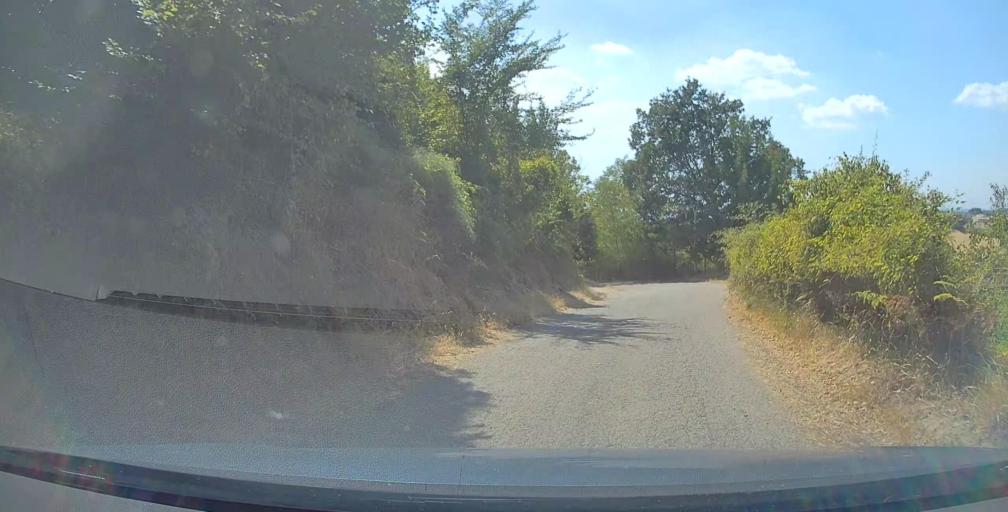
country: IT
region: Latium
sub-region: Provincia di Rieti
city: Collevecchio
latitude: 42.3689
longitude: 12.5598
